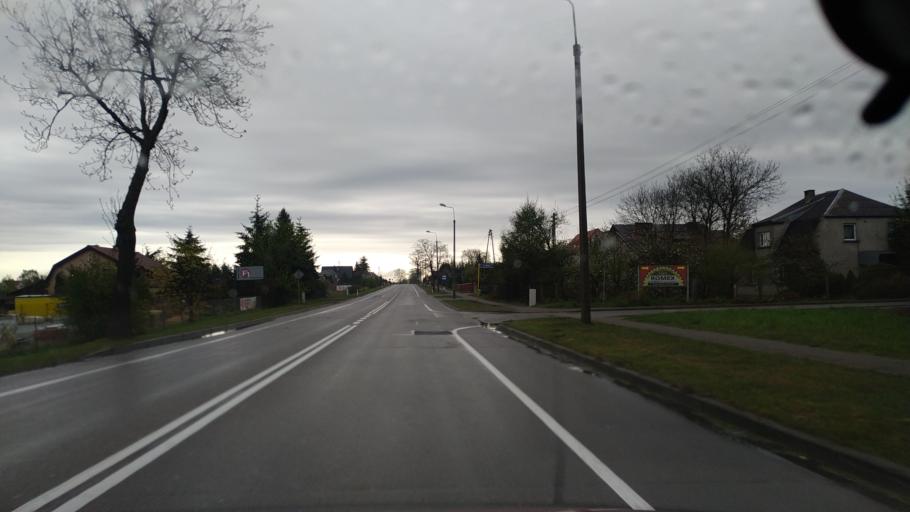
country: PL
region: Pomeranian Voivodeship
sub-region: Powiat chojnicki
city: Czersk
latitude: 53.7993
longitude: 17.9928
